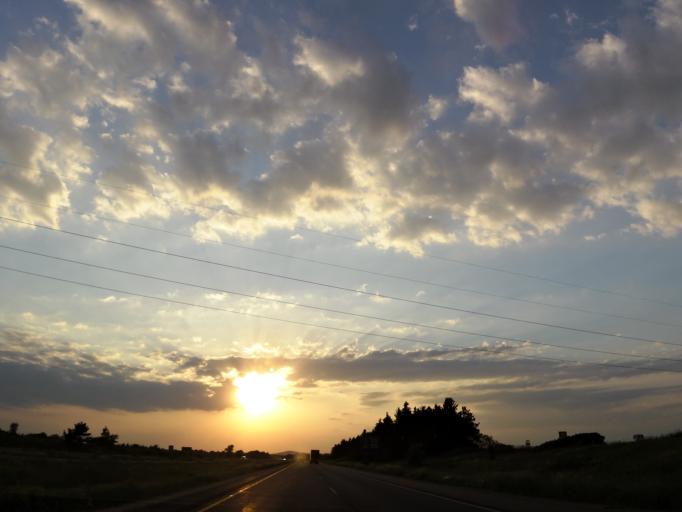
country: US
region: Wisconsin
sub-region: Eau Claire County
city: Eau Claire
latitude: 44.8372
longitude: -91.5905
